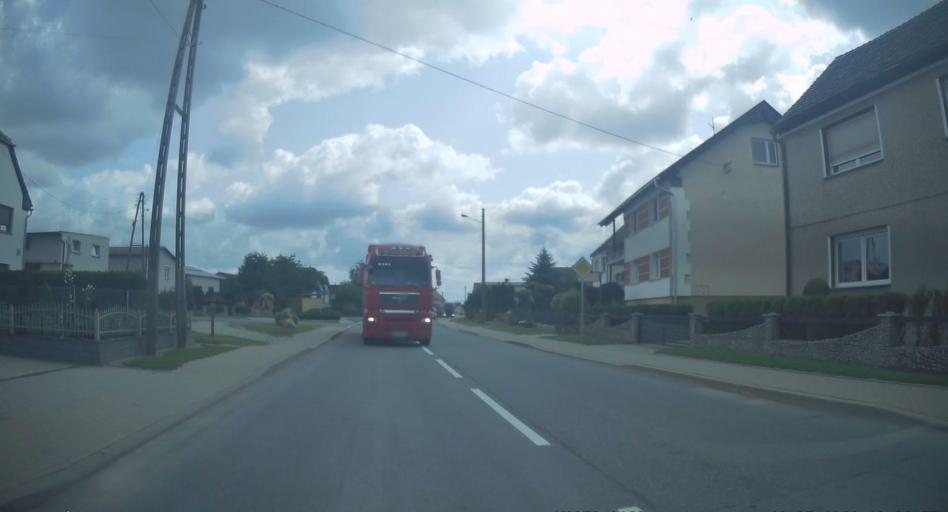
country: PL
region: Opole Voivodeship
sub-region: Powiat prudnicki
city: Twardawa
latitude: 50.3369
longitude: 17.9346
